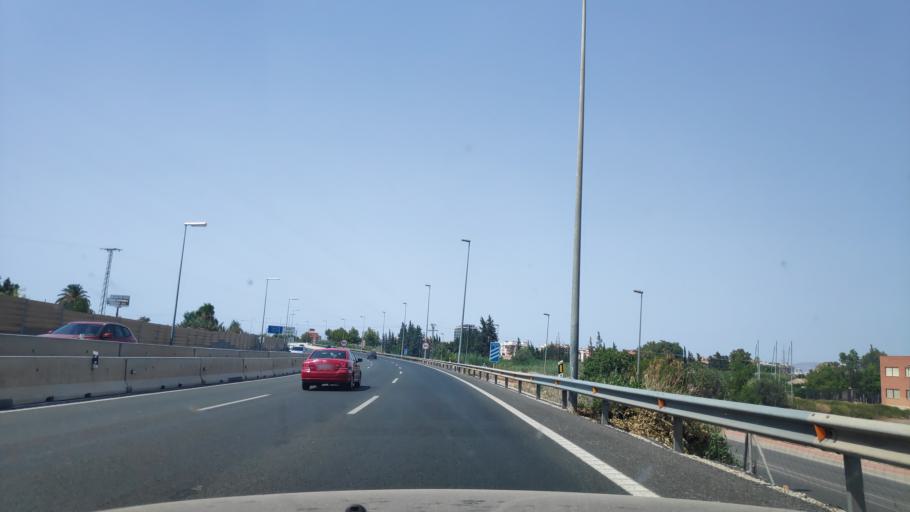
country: ES
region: Murcia
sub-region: Murcia
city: Murcia
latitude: 37.9608
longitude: -1.1350
